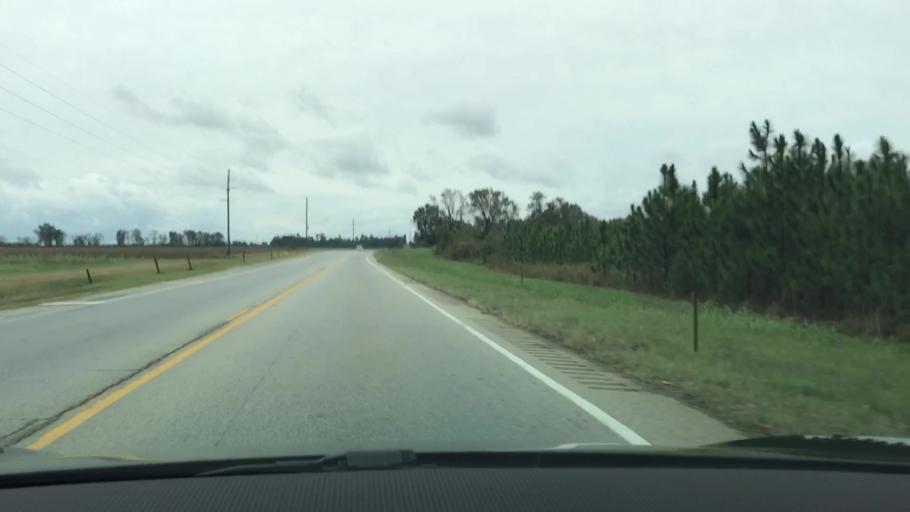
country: US
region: Georgia
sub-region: Jefferson County
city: Louisville
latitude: 33.0459
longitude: -82.4061
